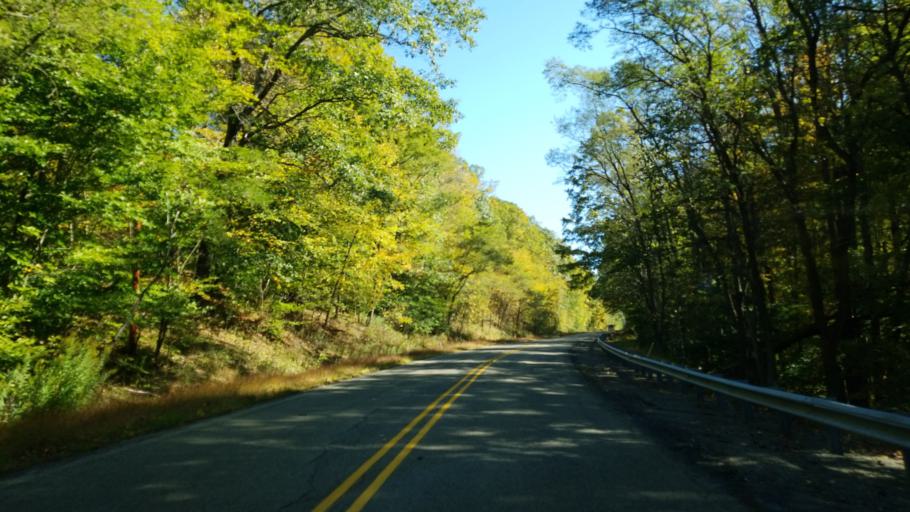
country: US
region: Pennsylvania
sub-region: Elk County
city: Saint Marys
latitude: 41.2622
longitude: -78.3912
